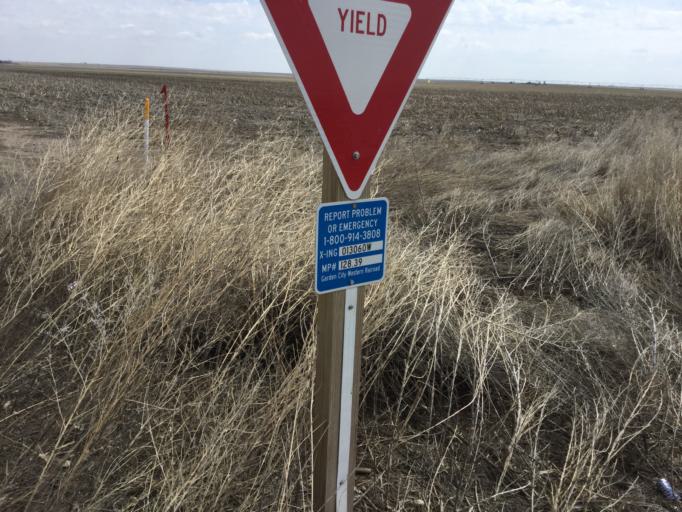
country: US
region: Kansas
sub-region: Scott County
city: Scott City
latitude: 38.3664
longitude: -100.9151
